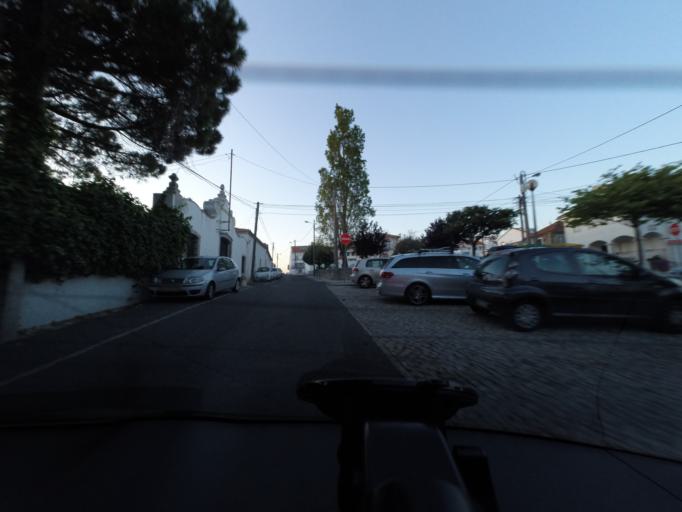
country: PT
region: Lisbon
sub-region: Cascais
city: Sao Domingos de Rana
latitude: 38.6992
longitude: -9.3311
